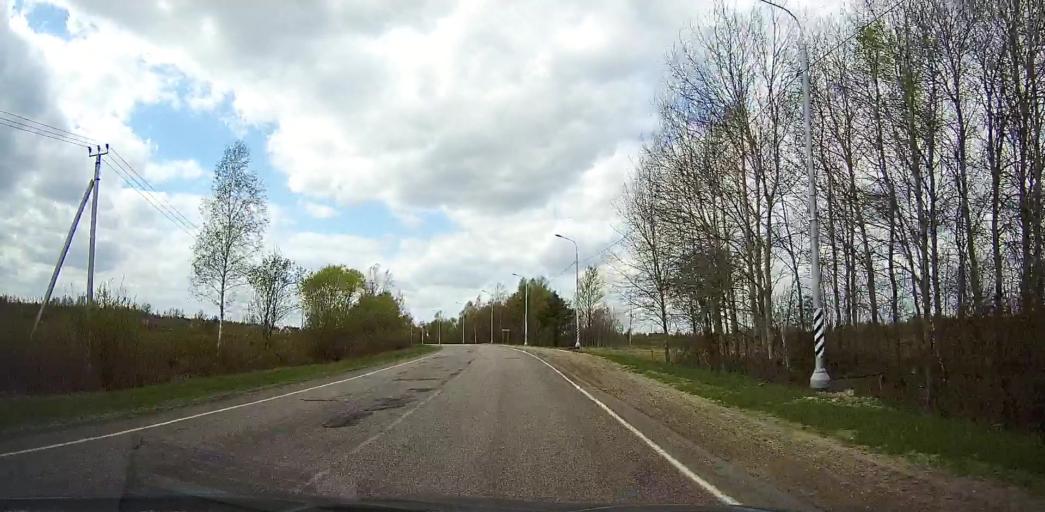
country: RU
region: Moskovskaya
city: Davydovo
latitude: 55.6633
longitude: 38.8053
